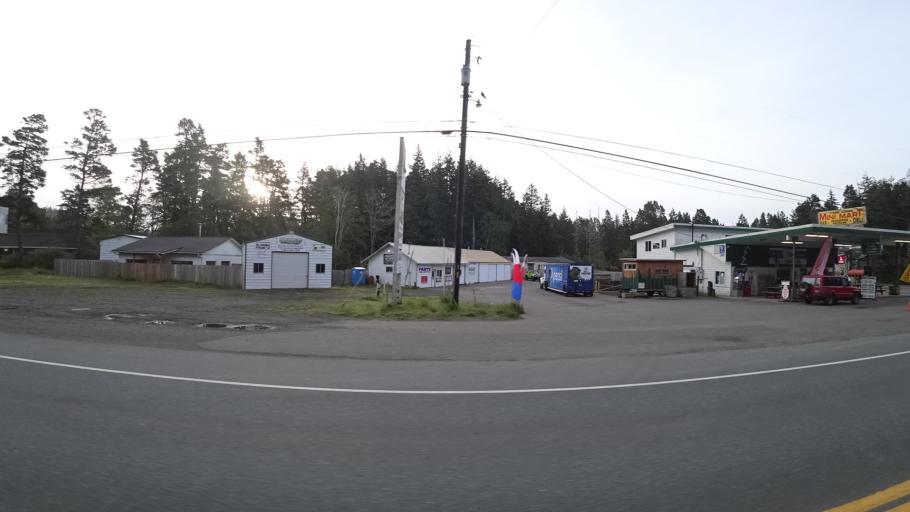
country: US
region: Oregon
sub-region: Coos County
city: Lakeside
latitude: 43.5951
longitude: -124.1816
